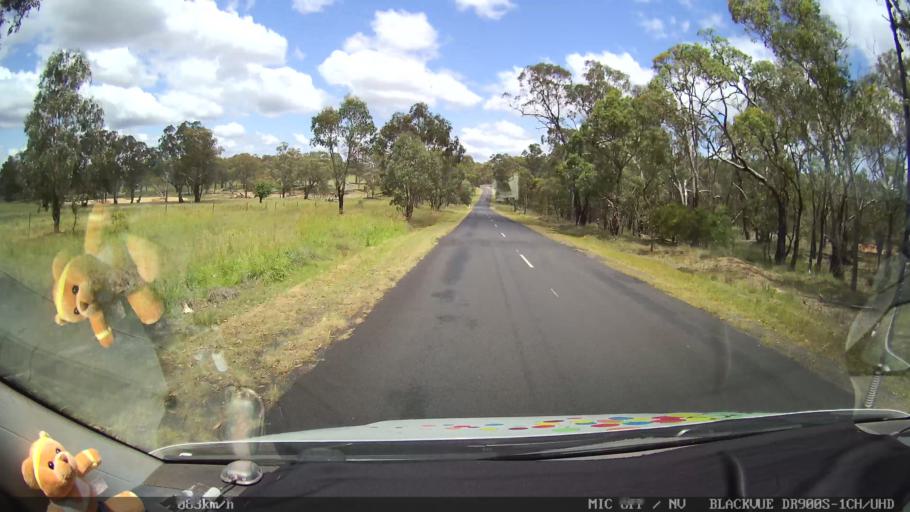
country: AU
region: New South Wales
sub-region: Glen Innes Severn
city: Glen Innes
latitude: -29.4684
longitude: 151.6317
